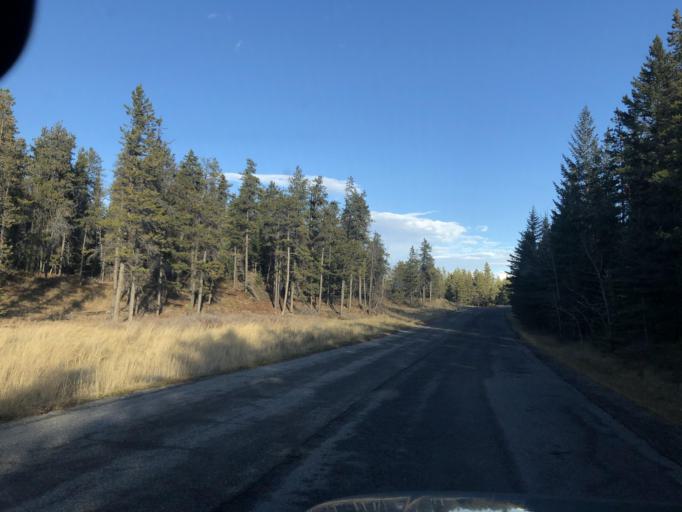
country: CA
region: Alberta
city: Canmore
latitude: 51.0767
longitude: -115.0677
